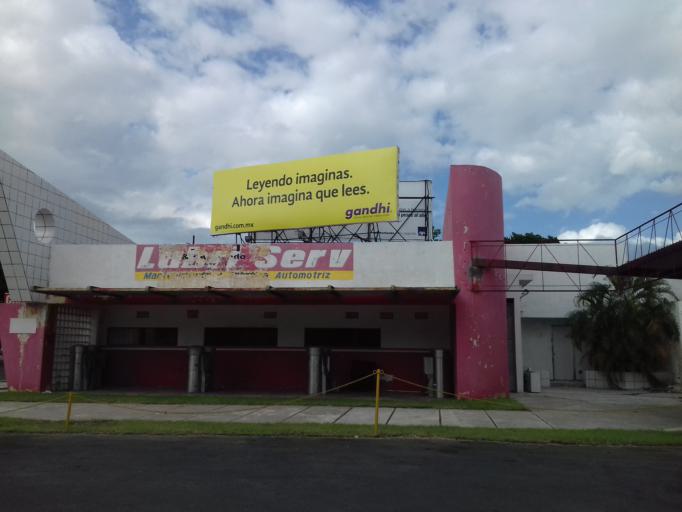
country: MX
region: Yucatan
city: Merida
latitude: 20.9950
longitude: -89.6161
